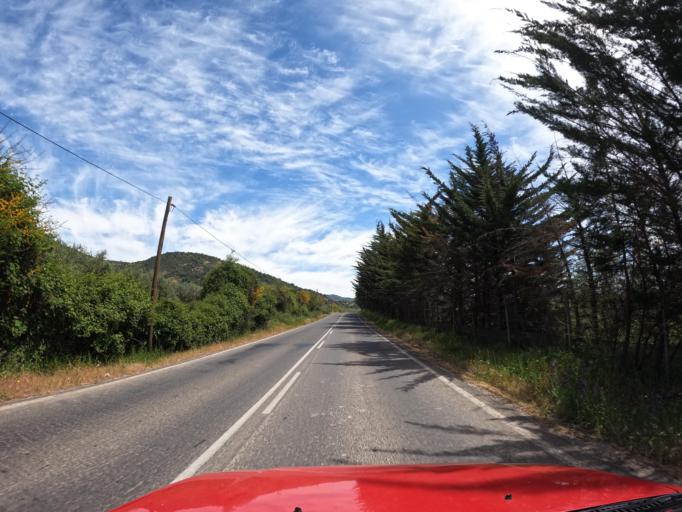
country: CL
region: Maule
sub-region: Provincia de Talca
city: Talca
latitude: -35.1204
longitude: -71.6485
